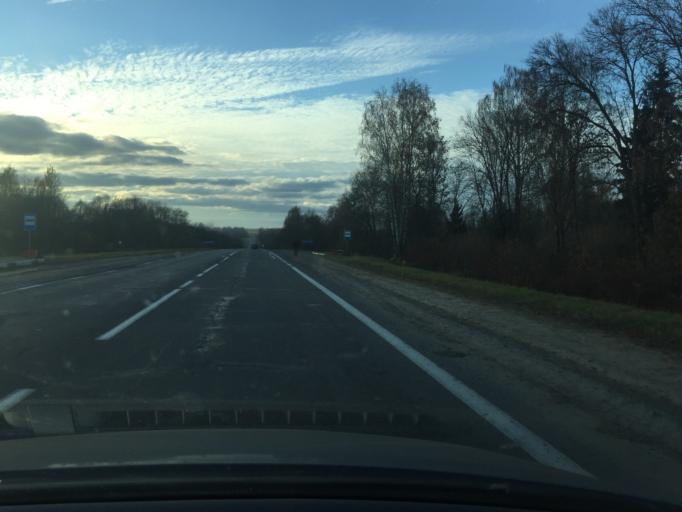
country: BY
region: Vitebsk
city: Vyerkhnyadzvinsk
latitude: 55.8376
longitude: 27.8914
